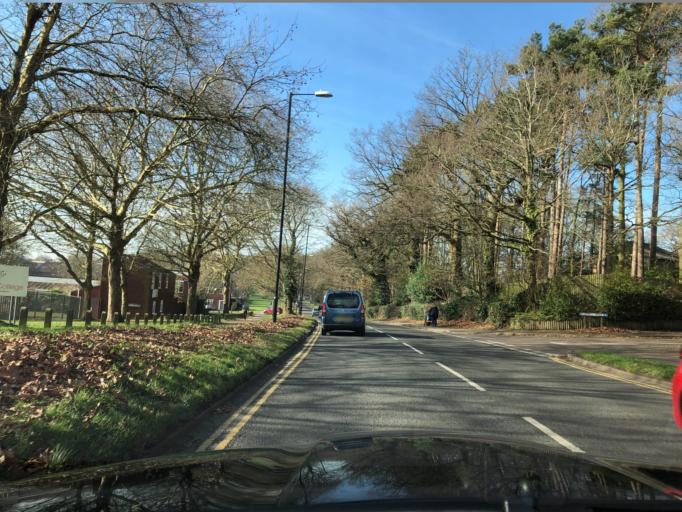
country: GB
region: England
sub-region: Warwickshire
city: Kenilworth
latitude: 52.4021
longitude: -1.5767
